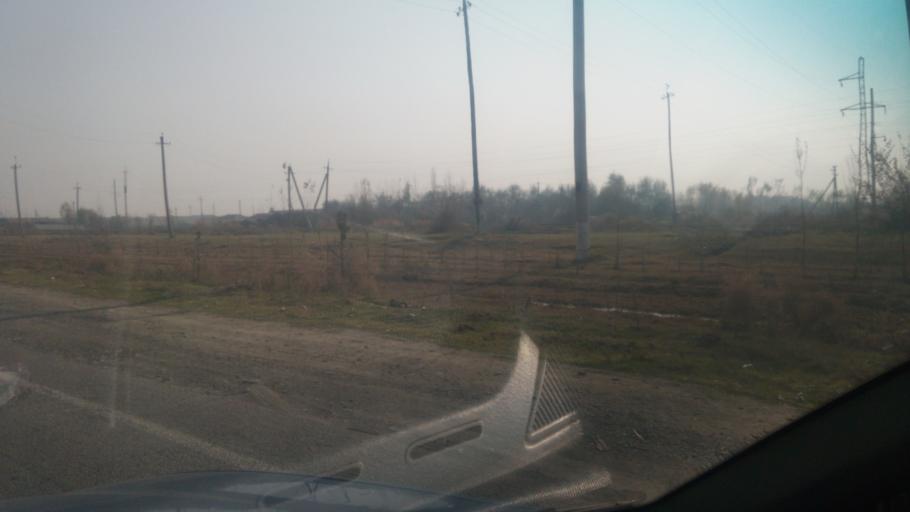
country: UZ
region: Sirdaryo
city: Guliston
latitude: 40.4884
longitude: 68.7501
